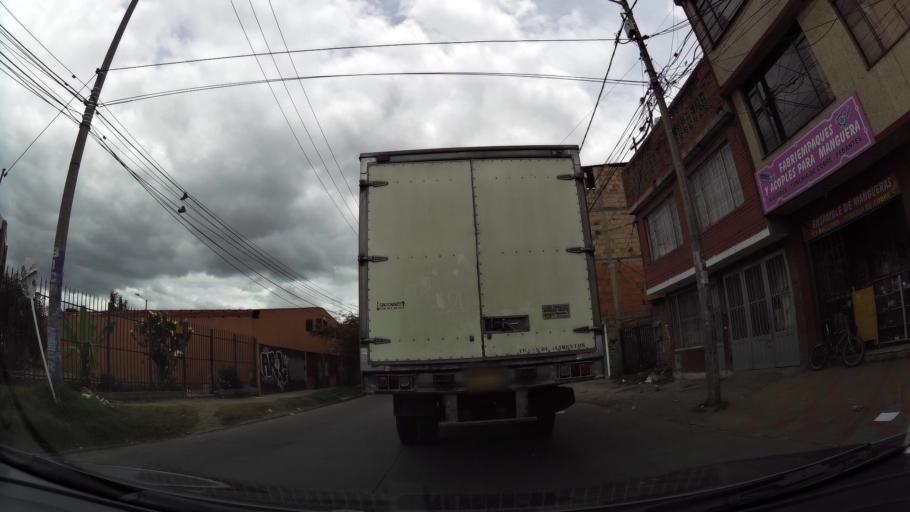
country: CO
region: Cundinamarca
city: Funza
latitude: 4.7100
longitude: -74.1254
